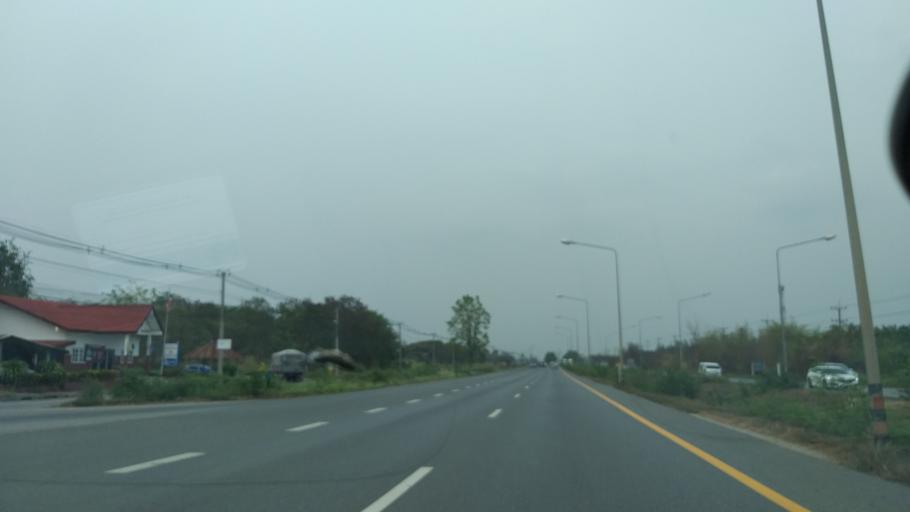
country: TH
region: Chon Buri
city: Ban Bueng
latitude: 13.2898
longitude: 101.2582
